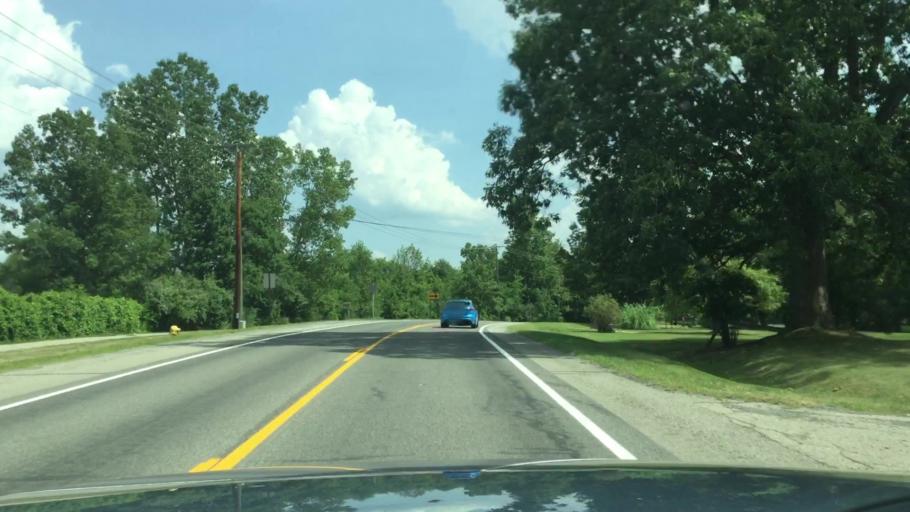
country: US
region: Michigan
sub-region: Washtenaw County
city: Ypsilanti
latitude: 42.2044
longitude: -83.6110
